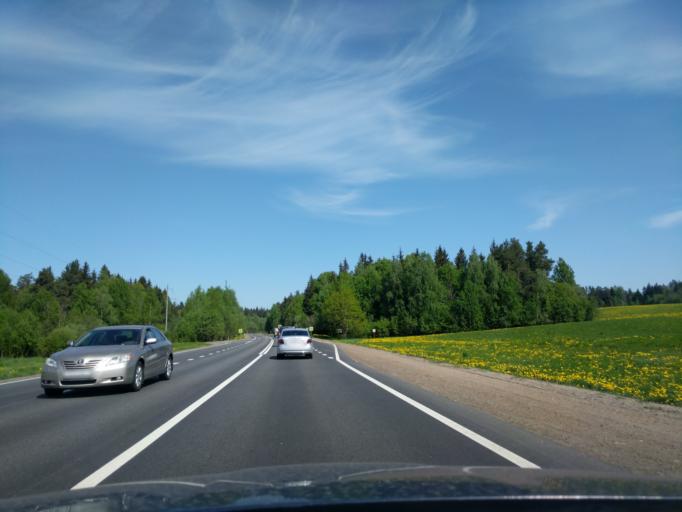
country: BY
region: Minsk
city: Bal'shavik
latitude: 54.1015
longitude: 27.5330
